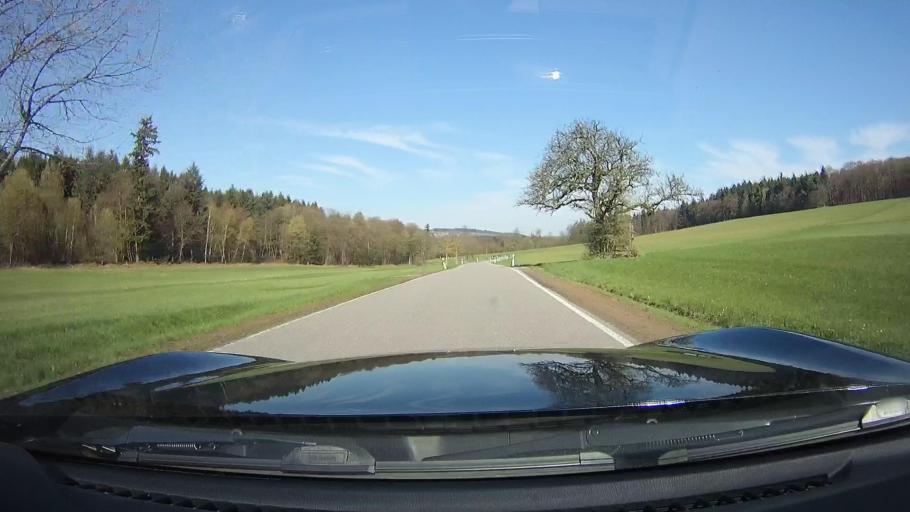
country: DE
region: Baden-Wuerttemberg
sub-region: Karlsruhe Region
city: Neunkirchen
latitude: 49.4057
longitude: 8.9700
